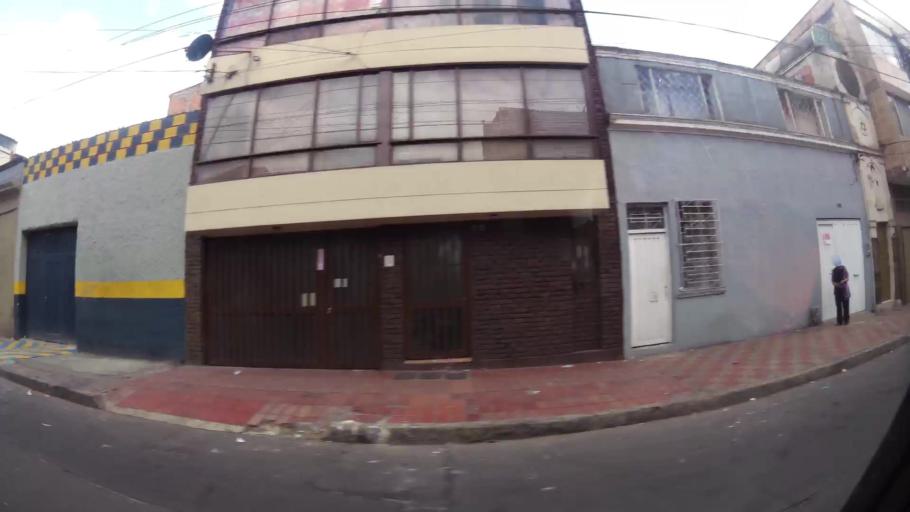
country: CO
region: Bogota D.C.
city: Bogota
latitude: 4.6370
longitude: -74.0703
